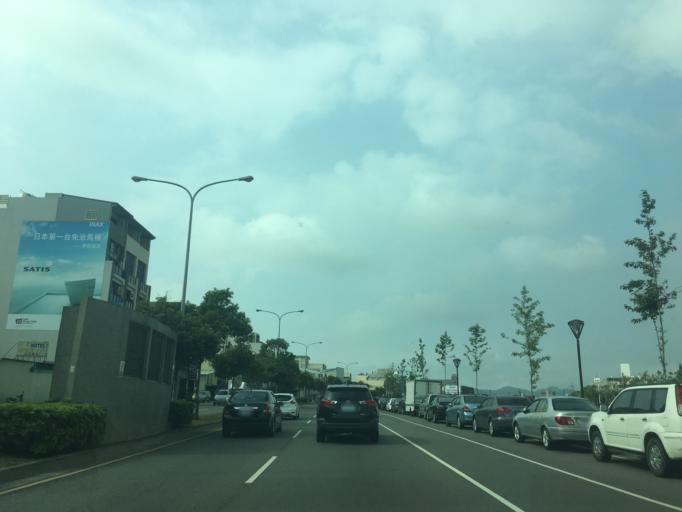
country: TW
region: Taiwan
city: Fengyuan
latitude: 24.2404
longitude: 120.7283
